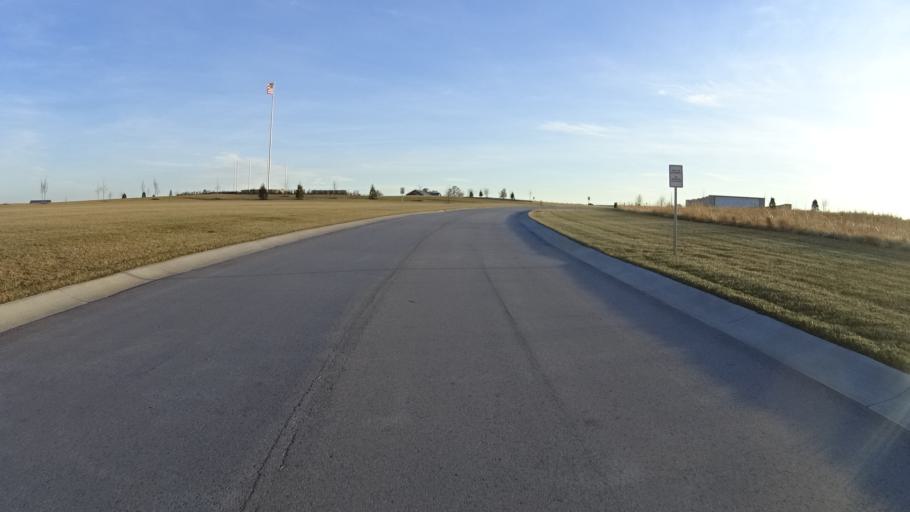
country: US
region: Nebraska
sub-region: Sarpy County
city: Chalco
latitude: 41.1382
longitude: -96.1340
